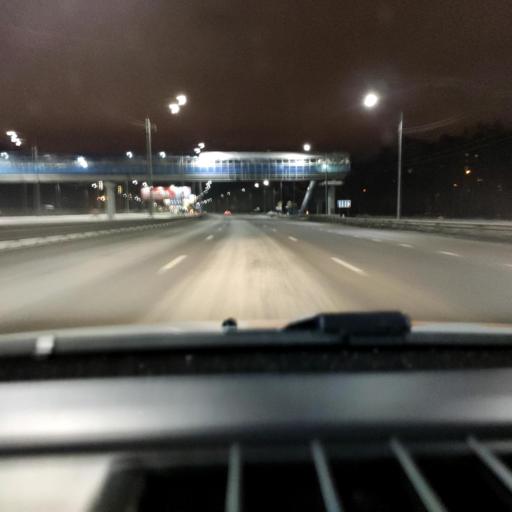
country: RU
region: Voronezj
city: Podgornoye
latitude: 51.7293
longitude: 39.1781
